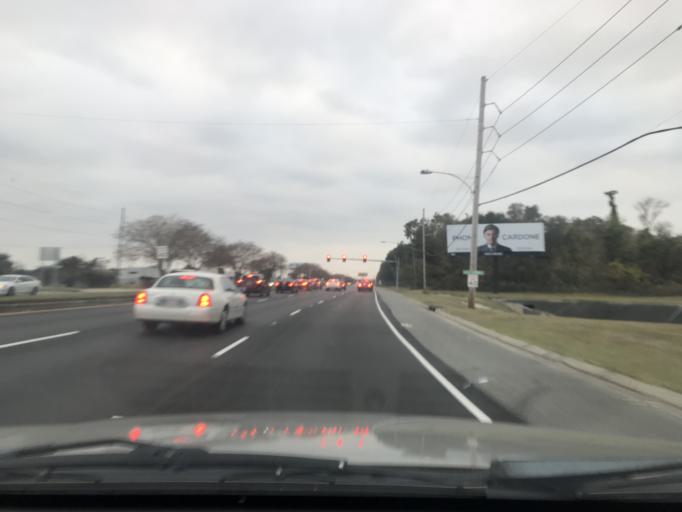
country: US
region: Louisiana
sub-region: Jefferson Parish
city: Woodmere
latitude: 29.8701
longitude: -90.0763
